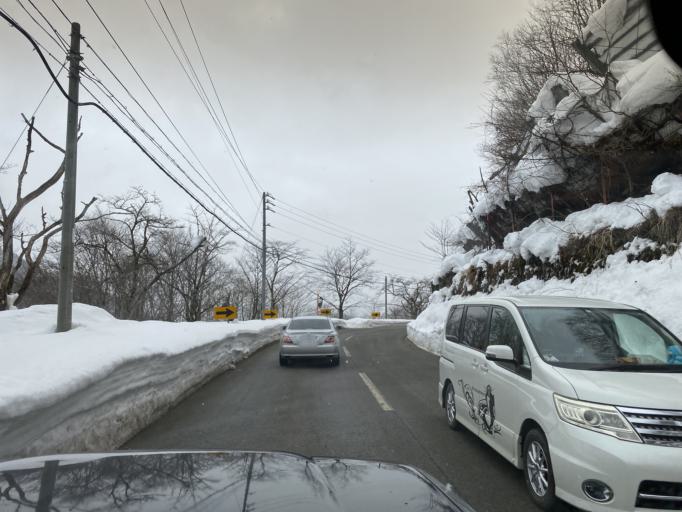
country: JP
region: Gifu
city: Takayama
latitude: 36.0970
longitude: 136.9357
